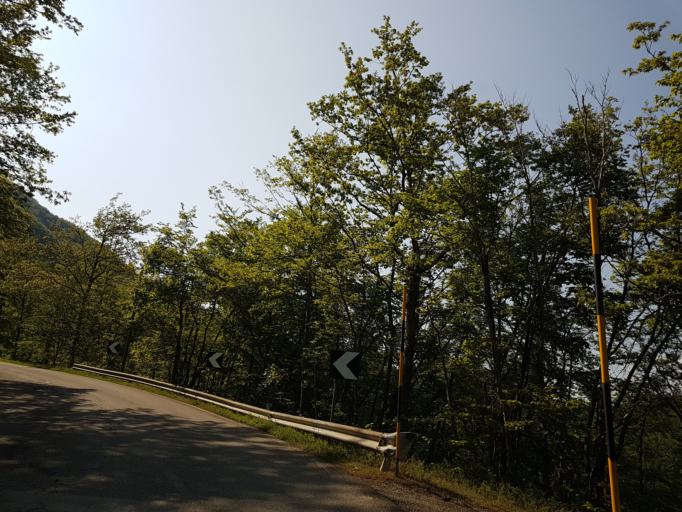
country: IT
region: Emilia-Romagna
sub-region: Forli-Cesena
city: San Piero in Bagno
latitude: 43.8121
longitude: 11.9227
